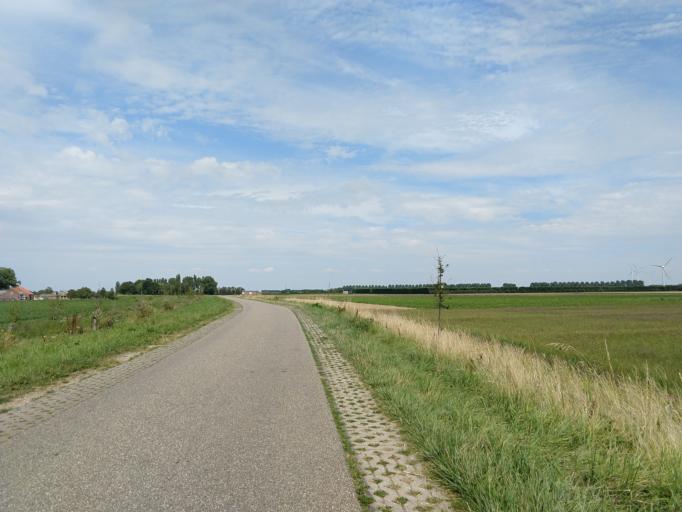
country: NL
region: Zeeland
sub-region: Gemeente Middelburg
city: Middelburg
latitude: 51.4834
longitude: 3.6767
